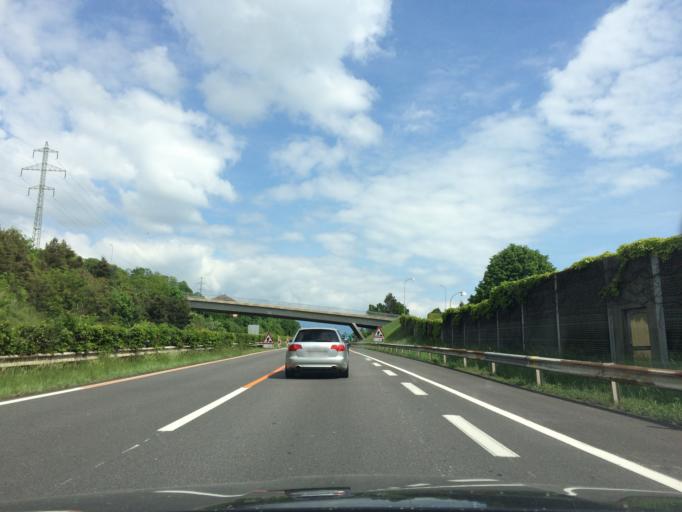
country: CH
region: Vaud
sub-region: Lavaux-Oron District
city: Chexbres
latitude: 46.4863
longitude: 6.7732
